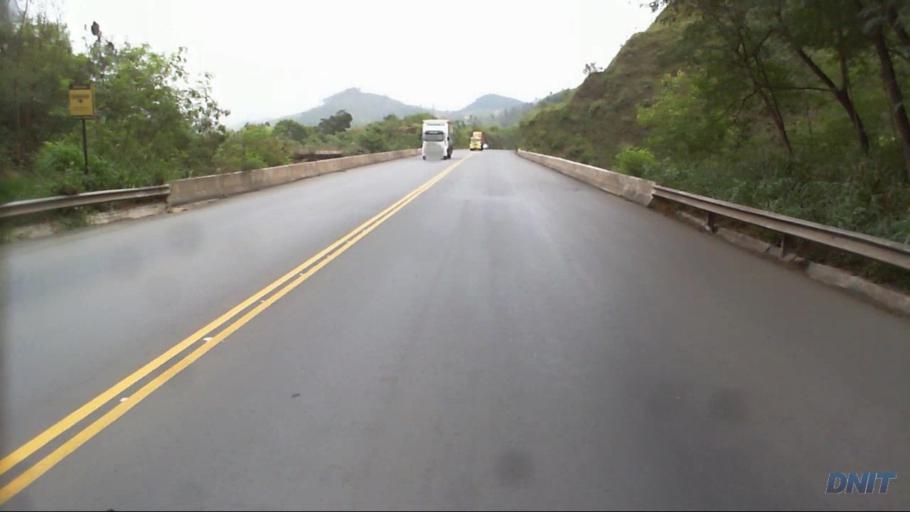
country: BR
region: Minas Gerais
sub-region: Coronel Fabriciano
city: Coronel Fabriciano
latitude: -19.5235
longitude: -42.6534
